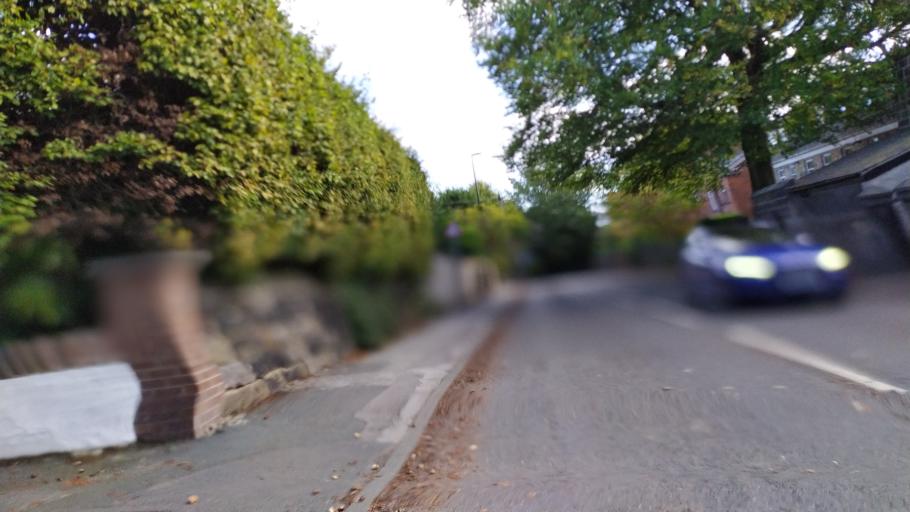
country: GB
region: England
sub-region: City and Borough of Leeds
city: Chapel Allerton
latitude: 53.8260
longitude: -1.5731
